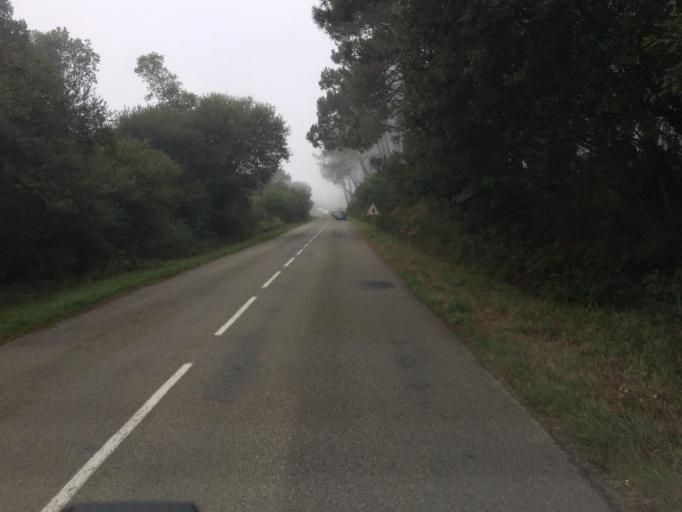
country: FR
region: Brittany
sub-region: Departement du Finistere
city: Plogoff
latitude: 48.0623
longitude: -4.6448
